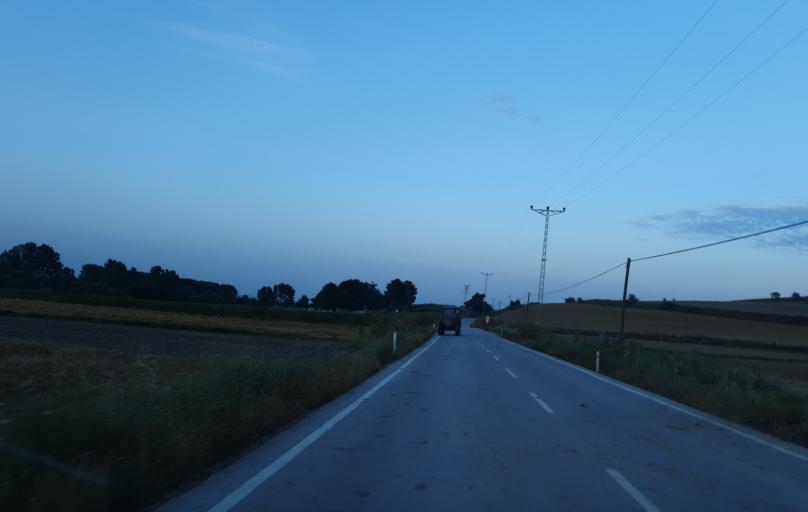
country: TR
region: Tekirdag
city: Velimese
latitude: 41.3493
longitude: 27.8731
